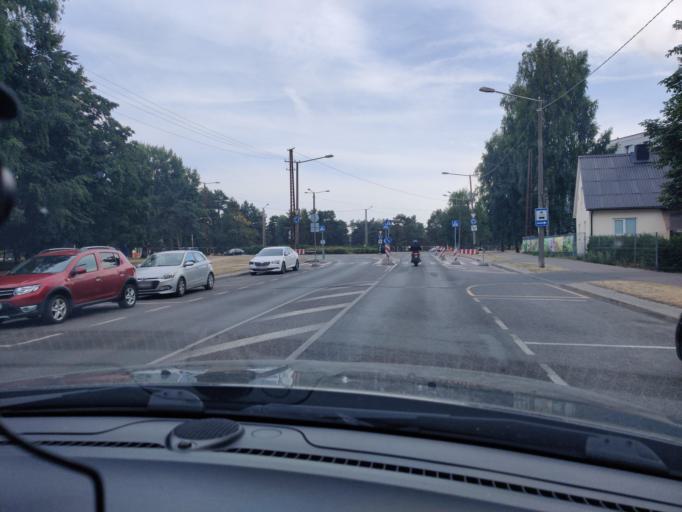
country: EE
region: Harju
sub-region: Saue vald
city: Laagri
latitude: 59.4021
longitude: 24.6783
